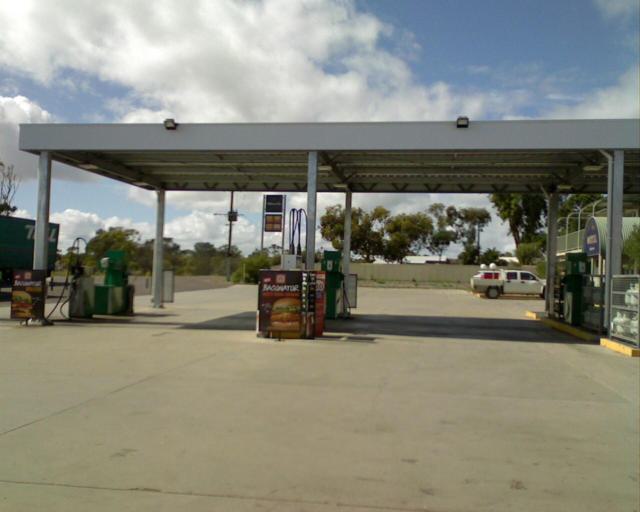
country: AU
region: South Australia
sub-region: Ceduna
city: Ceduna
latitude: -32.1138
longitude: 133.6728
